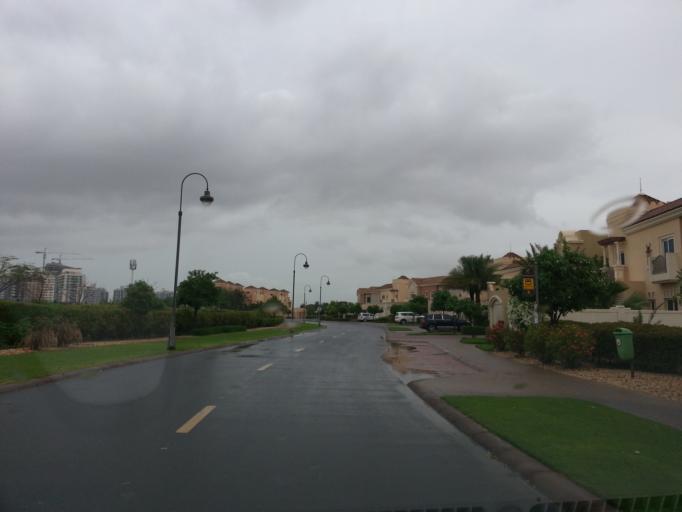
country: AE
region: Dubai
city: Dubai
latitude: 25.0309
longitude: 55.2084
